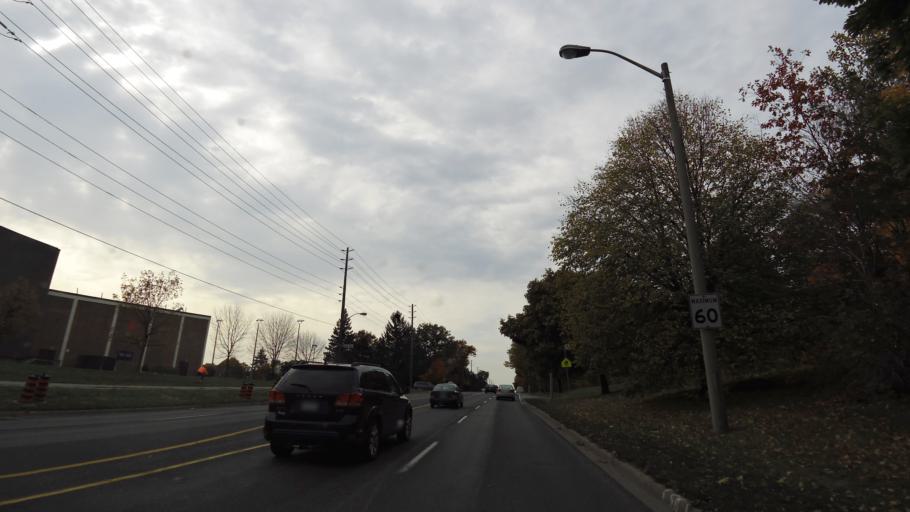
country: CA
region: Ontario
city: Etobicoke
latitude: 43.6796
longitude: -79.5400
